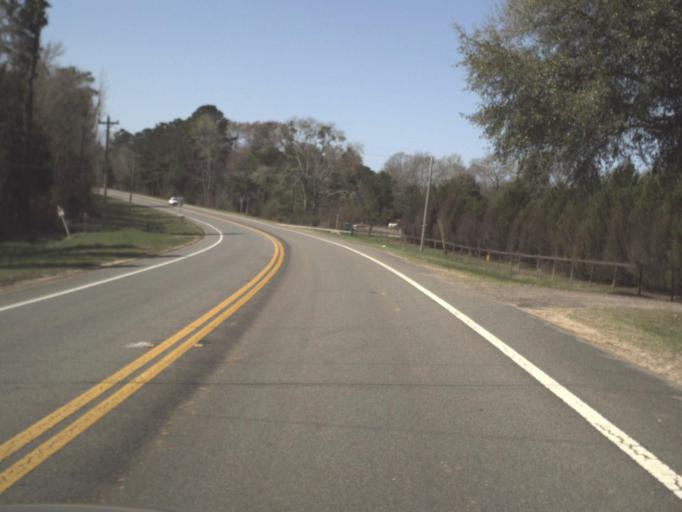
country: US
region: Florida
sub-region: Gadsden County
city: Havana
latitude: 30.6167
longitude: -84.4467
